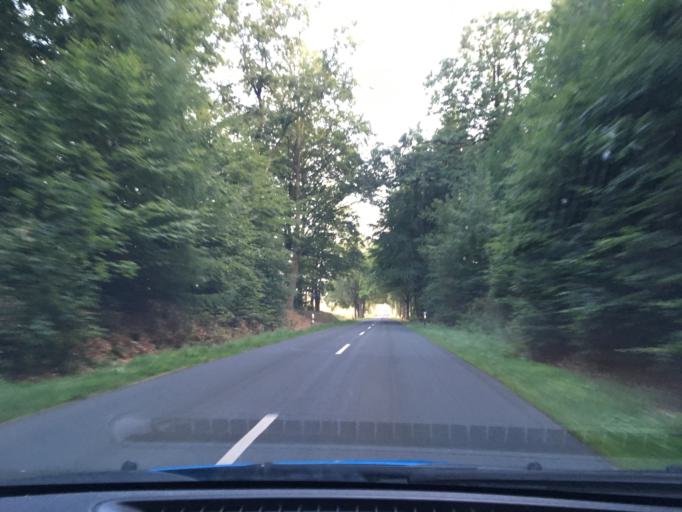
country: DE
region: Lower Saxony
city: Nahrendorf
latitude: 53.1911
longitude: 10.8167
